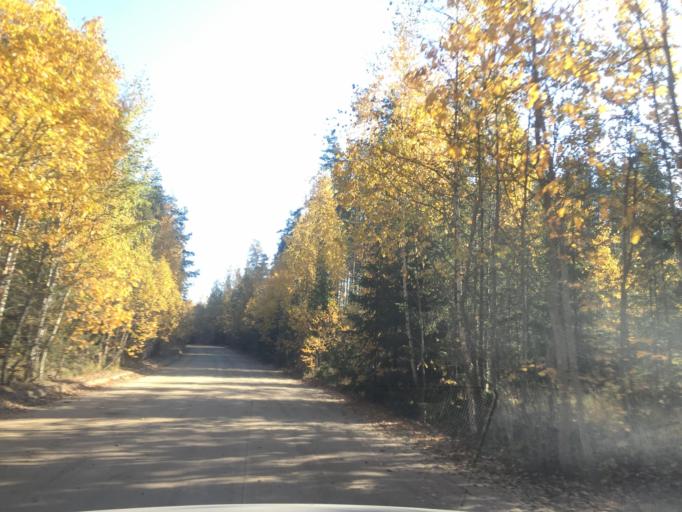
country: RU
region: Leningrad
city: Kuznechnoye
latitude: 61.3115
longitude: 30.0238
